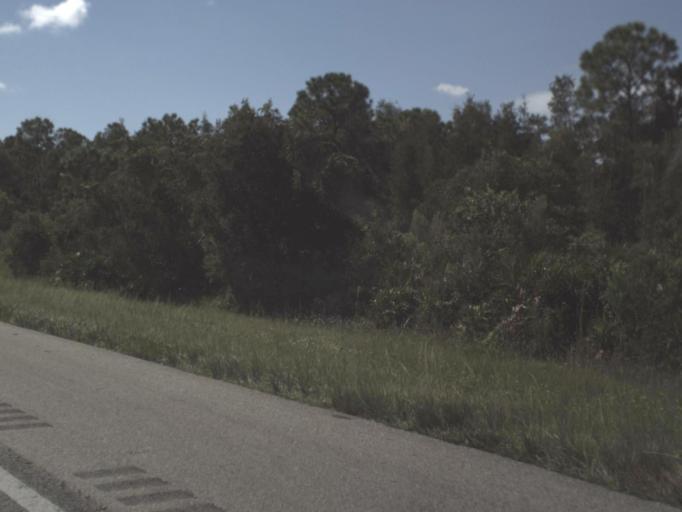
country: US
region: Florida
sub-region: Lee County
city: Burnt Store Marina
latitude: 26.8334
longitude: -81.9582
